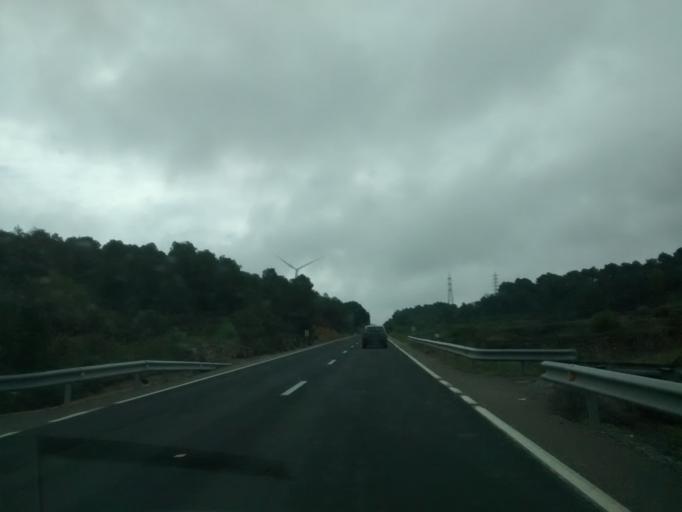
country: ES
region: Catalonia
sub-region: Provincia de Tarragona
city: Batea
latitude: 41.0609
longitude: 0.3519
